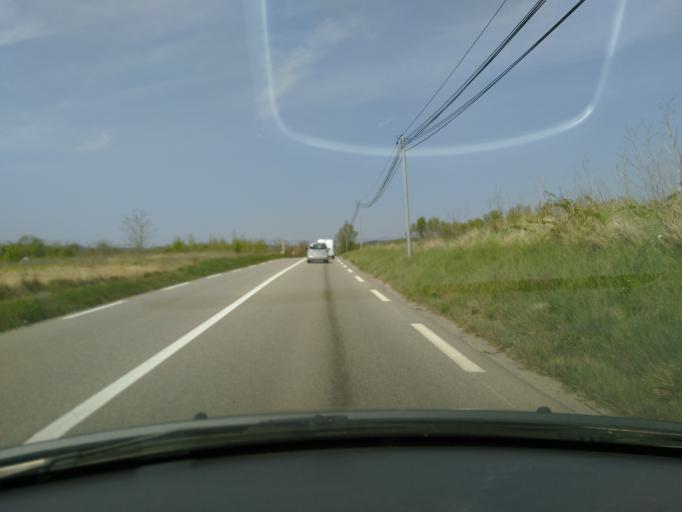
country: FR
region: Rhone-Alpes
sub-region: Departement de l'Ardeche
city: Saint-Sernin
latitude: 44.5309
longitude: 4.4181
